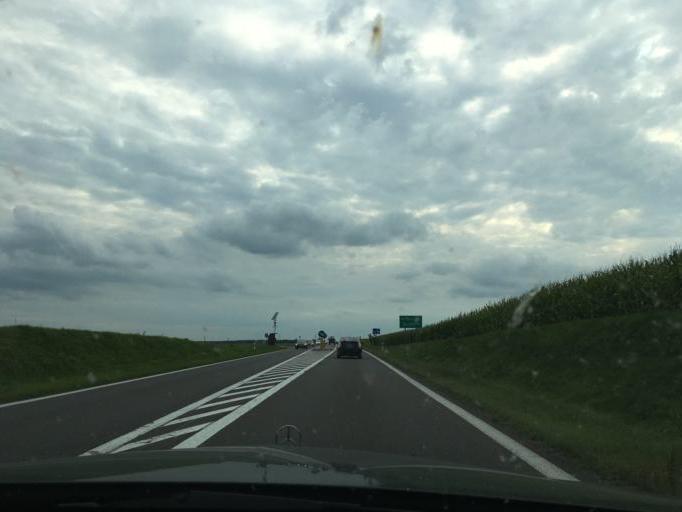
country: PL
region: Podlasie
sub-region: Powiat grajewski
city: Szczuczyn
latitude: 53.5014
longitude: 22.2333
